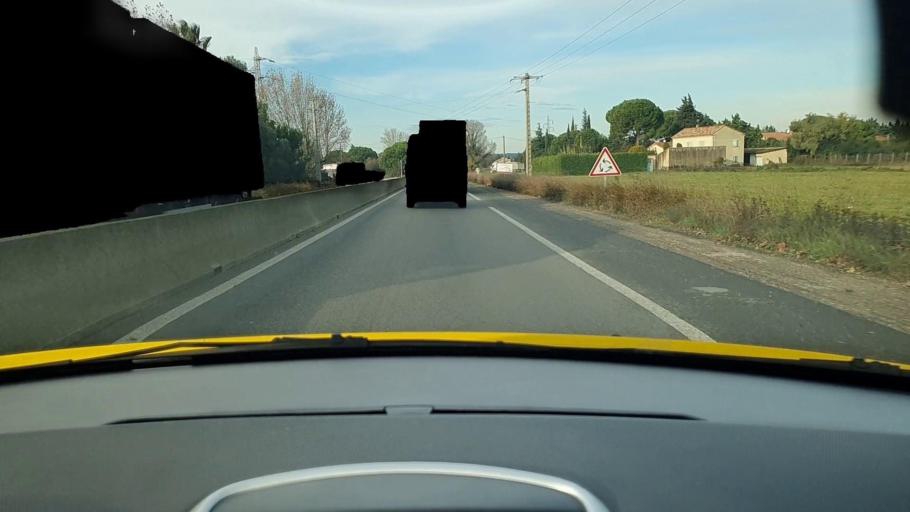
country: FR
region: Languedoc-Roussillon
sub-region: Departement du Gard
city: Beaucaire
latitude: 43.7922
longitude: 4.6324
